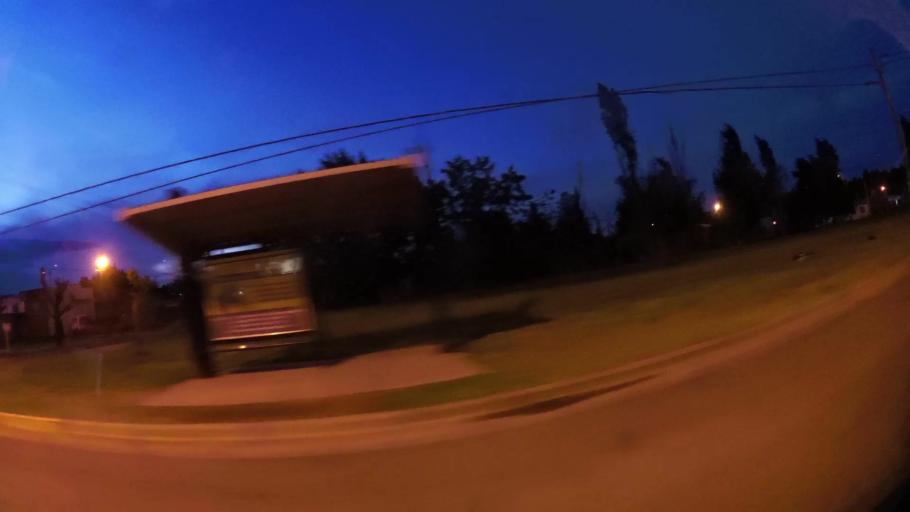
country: AR
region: Buenos Aires
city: San Nicolas de los Arroyos
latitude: -33.3626
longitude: -60.2518
